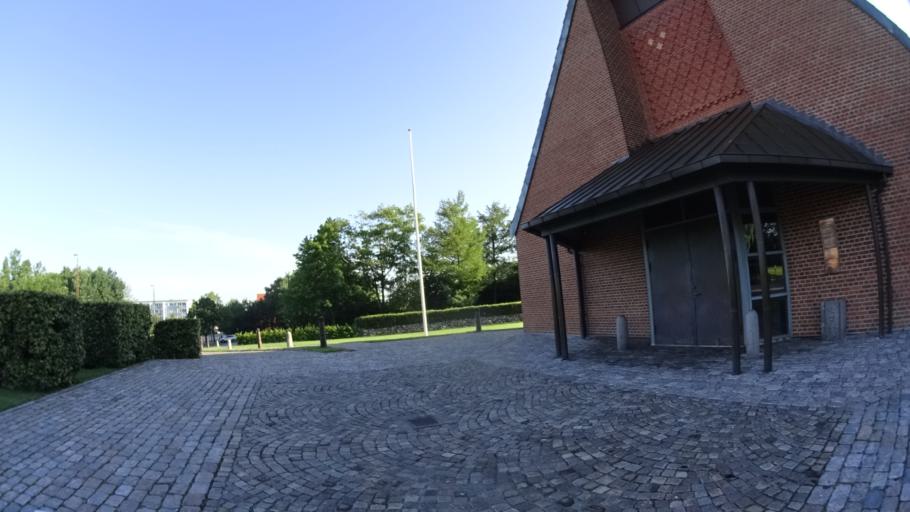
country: DK
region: Central Jutland
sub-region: Arhus Kommune
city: Arhus
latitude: 56.1291
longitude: 10.1831
